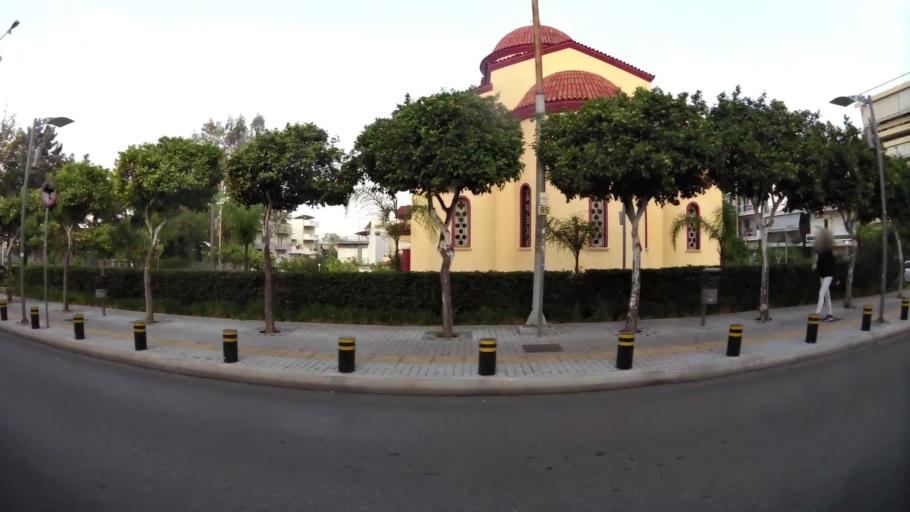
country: GR
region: Attica
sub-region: Nomarchia Athinas
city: Ymittos
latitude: 37.9499
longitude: 23.7453
